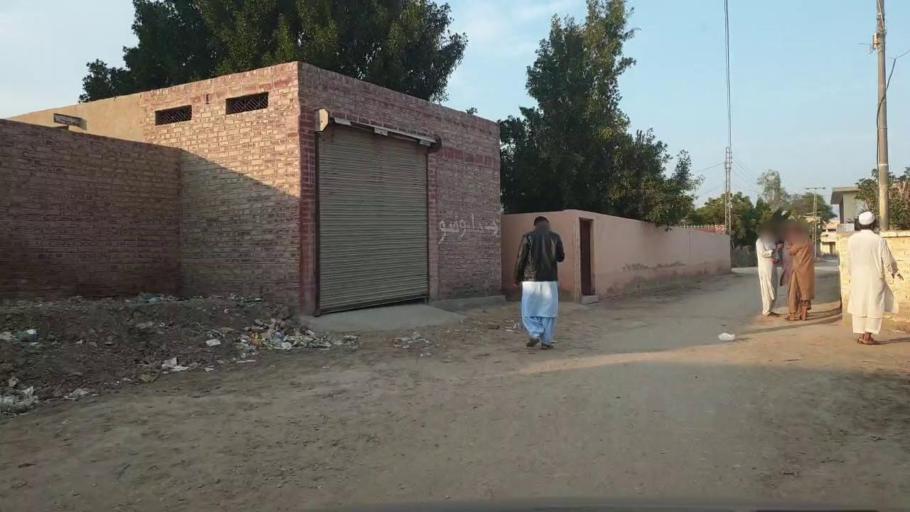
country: PK
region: Sindh
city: Shahpur Chakar
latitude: 26.1639
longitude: 68.6267
